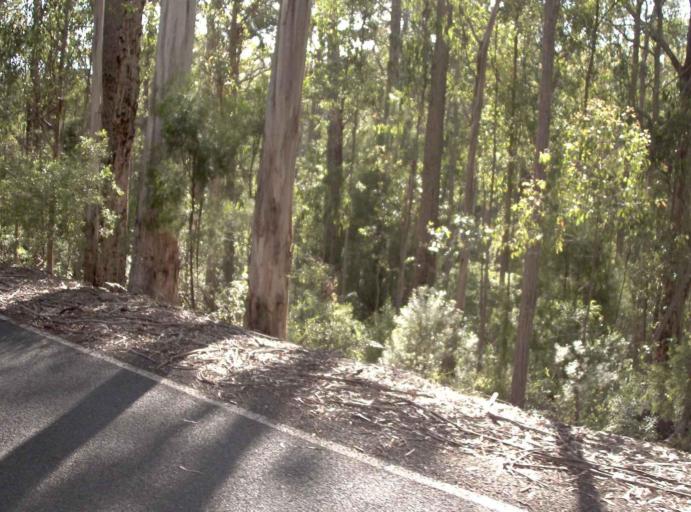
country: AU
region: Victoria
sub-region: East Gippsland
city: Lakes Entrance
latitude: -37.5864
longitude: 148.5352
